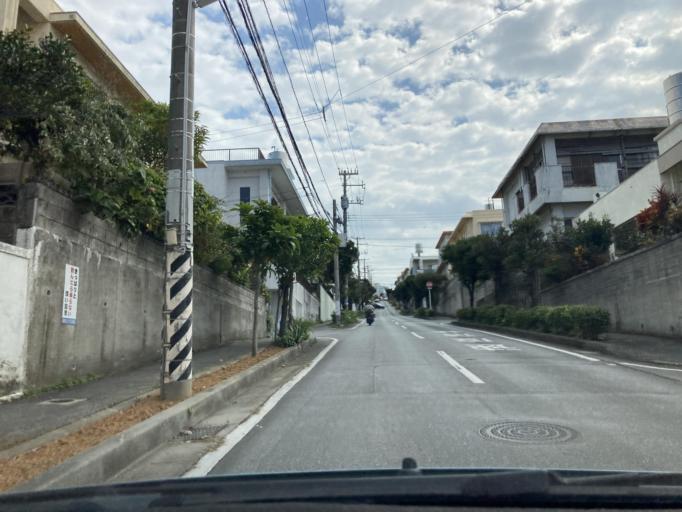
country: JP
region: Okinawa
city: Tomigusuku
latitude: 26.1887
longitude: 127.6944
